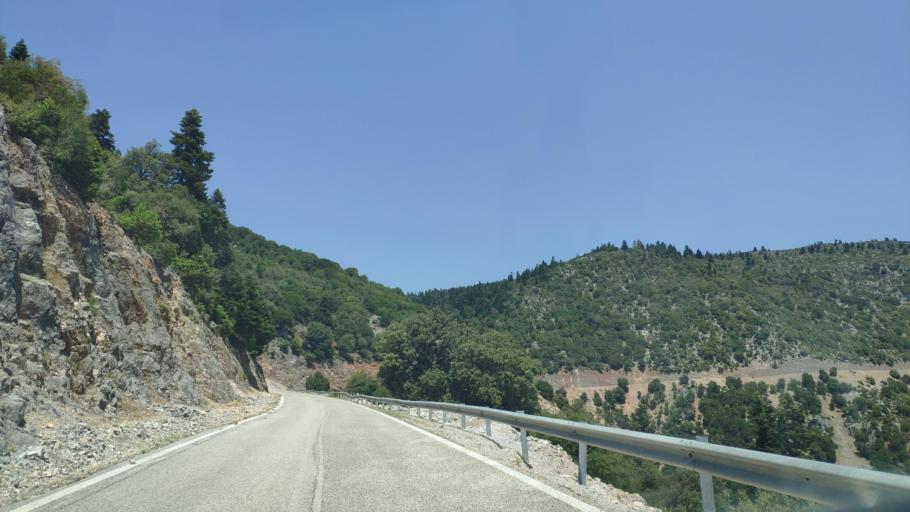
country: GR
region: West Greece
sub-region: Nomos Aitolias kai Akarnanias
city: Krikellos
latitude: 39.0286
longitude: 21.3700
